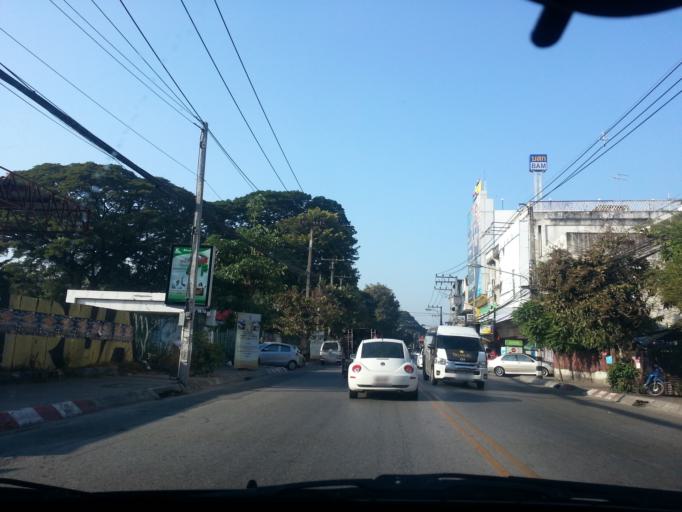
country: TH
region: Chiang Mai
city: Chiang Mai
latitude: 18.8003
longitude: 99.0132
